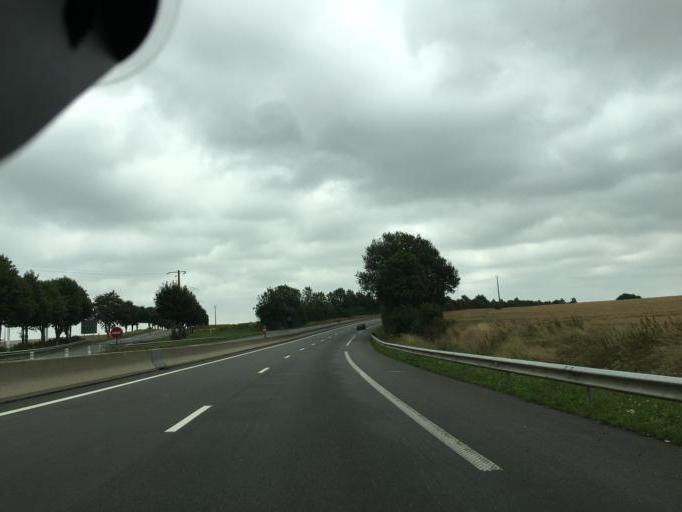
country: FR
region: Nord-Pas-de-Calais
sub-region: Departement du Pas-de-Calais
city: Saint-Pol-sur-Ternoise
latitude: 50.3769
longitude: 2.2959
